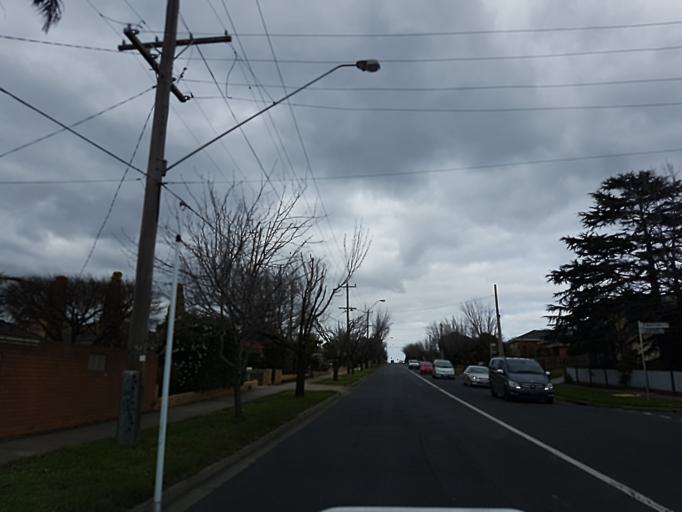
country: AU
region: Victoria
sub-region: Whitehorse
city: Blackburn North
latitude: -37.8048
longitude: 145.1414
